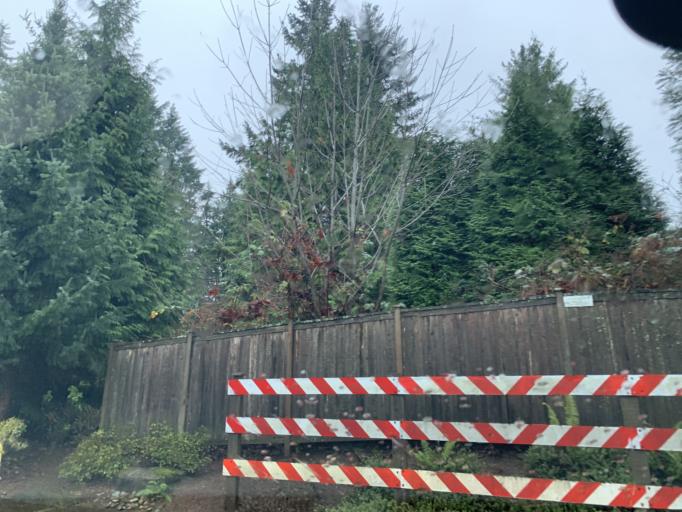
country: US
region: Washington
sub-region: King County
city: Kingsgate
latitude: 47.7385
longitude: -122.1689
